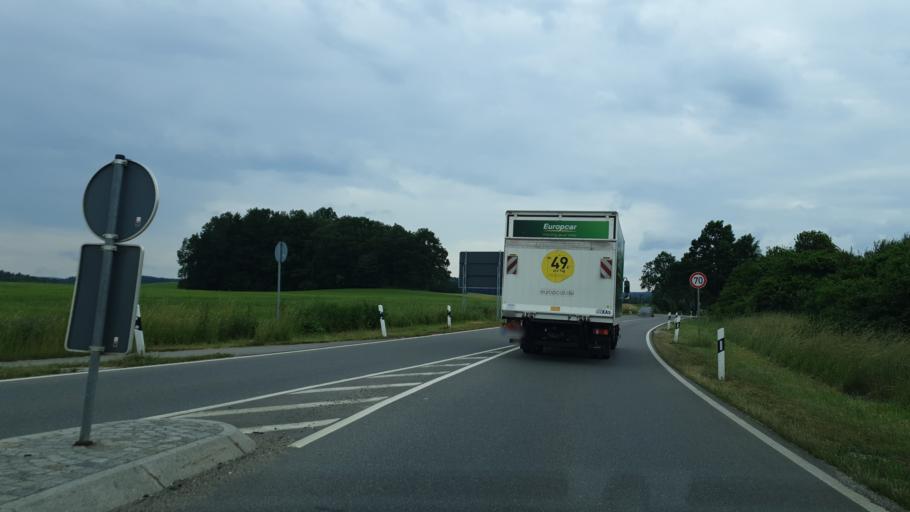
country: DE
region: Saxony
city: Waldkirchen
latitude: 50.5741
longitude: 12.3897
